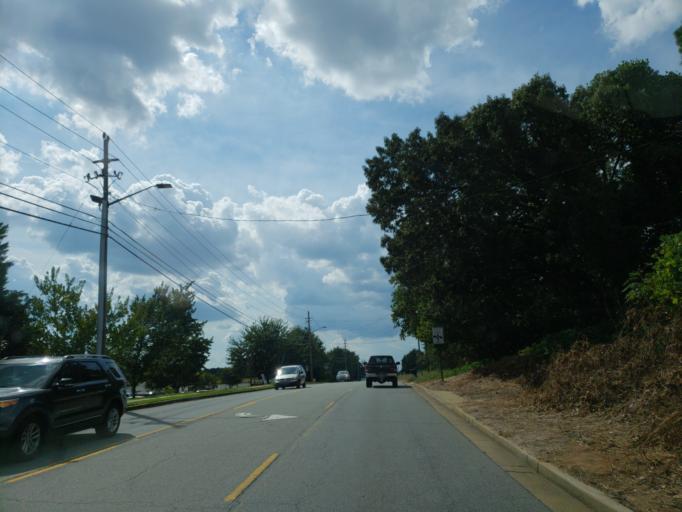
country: US
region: Georgia
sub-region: Cobb County
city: Acworth
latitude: 34.0754
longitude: -84.6465
